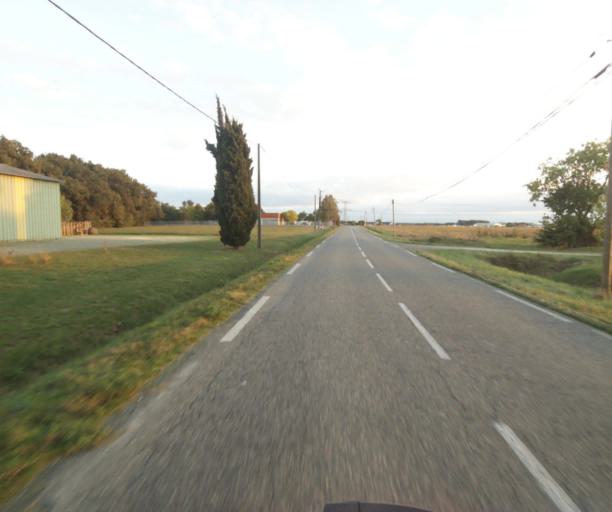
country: FR
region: Midi-Pyrenees
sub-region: Departement du Tarn-et-Garonne
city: Verdun-sur-Garonne
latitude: 43.8285
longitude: 1.2434
